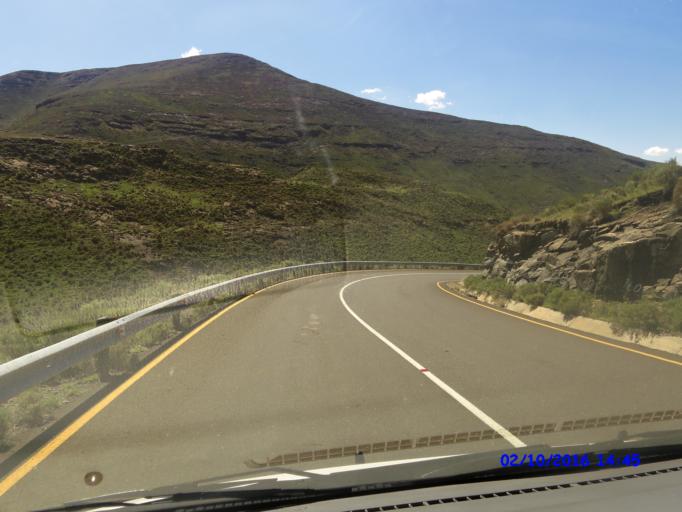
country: LS
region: Maseru
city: Nako
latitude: -29.5226
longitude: 28.0615
